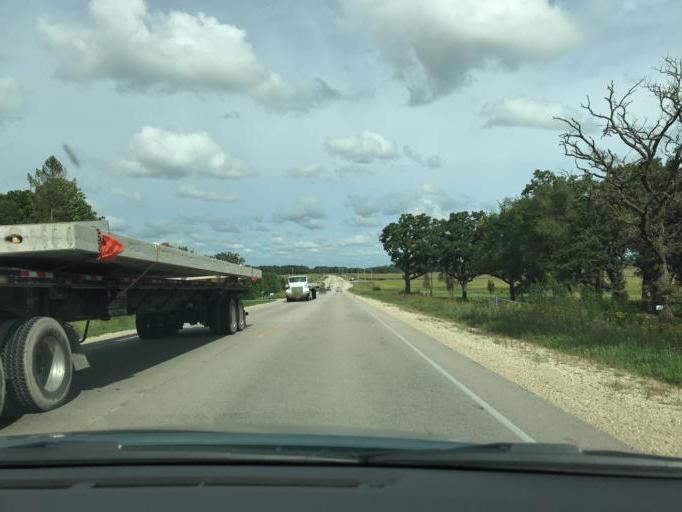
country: US
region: Wisconsin
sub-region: Racine County
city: Bohners Lake
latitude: 42.6075
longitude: -88.2271
